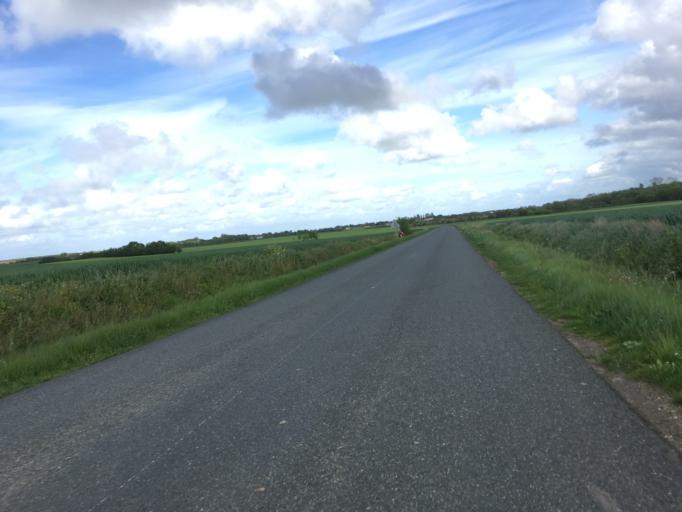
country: FR
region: Poitou-Charentes
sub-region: Departement de la Charente-Maritime
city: Verines
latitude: 46.1760
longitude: -0.9741
